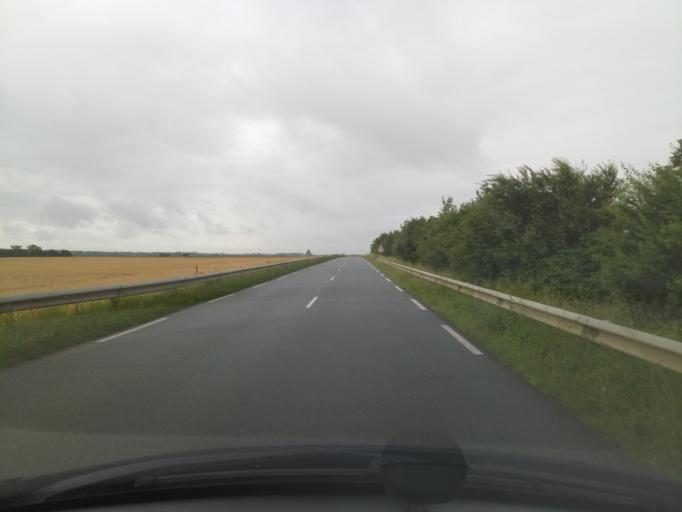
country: FR
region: Poitou-Charentes
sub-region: Departement de la Charente-Maritime
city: Saint-Jean-de-Liversay
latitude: 46.2050
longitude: -0.8734
